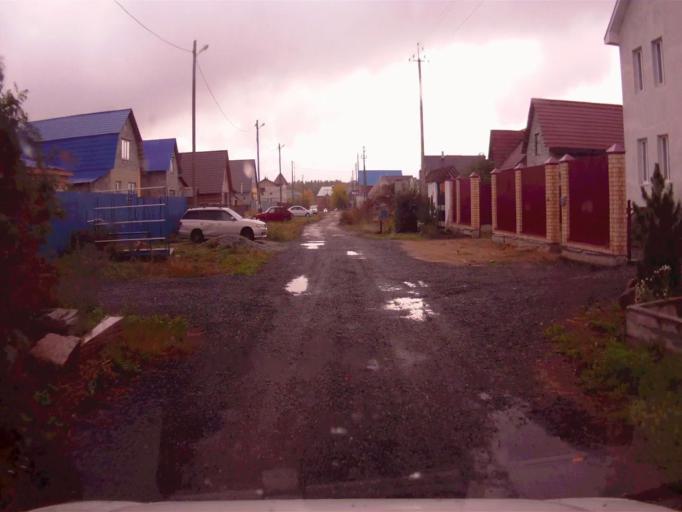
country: RU
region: Chelyabinsk
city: Dolgoderevenskoye
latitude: 55.3065
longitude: 61.3415
